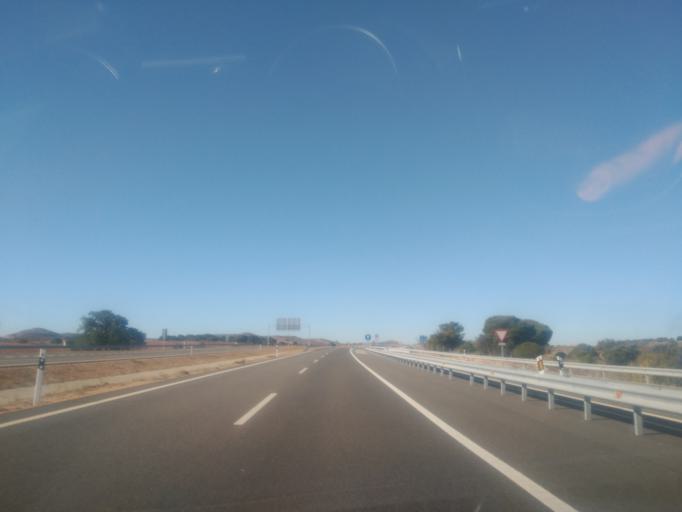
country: ES
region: Castille and Leon
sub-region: Provincia de Burgos
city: Fuentespina
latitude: 41.6364
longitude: -3.7093
